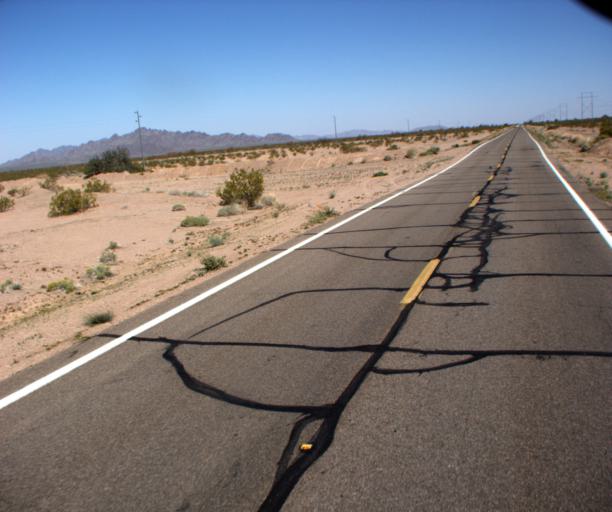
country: US
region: Arizona
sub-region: La Paz County
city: Quartzsite
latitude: 33.4254
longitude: -114.2170
